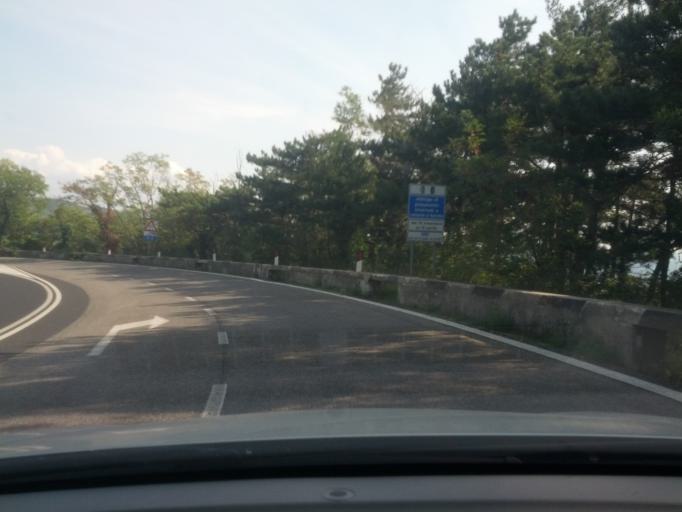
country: IT
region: Friuli Venezia Giulia
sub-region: Provincia di Trieste
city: Villa Opicina
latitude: 45.6674
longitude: 13.7906
